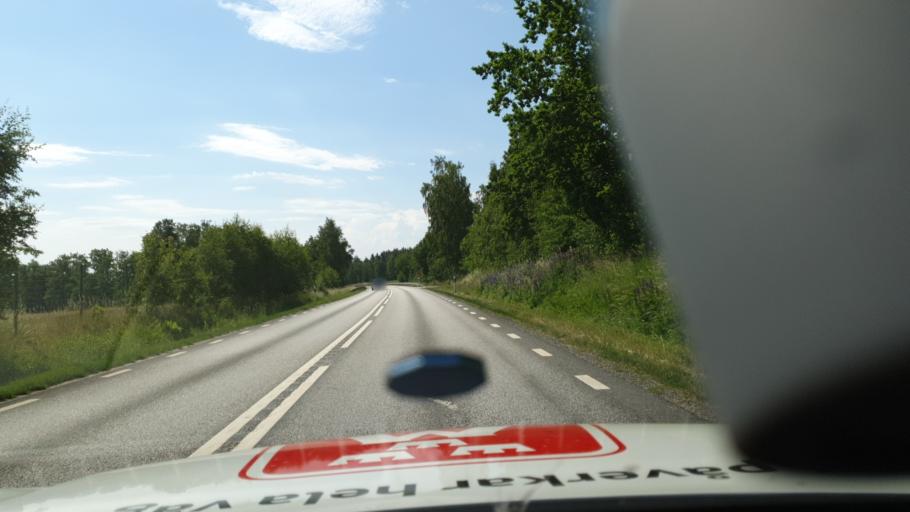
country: SE
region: Joenkoeping
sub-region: Habo Kommun
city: Habo
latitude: 58.0800
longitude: 14.1944
